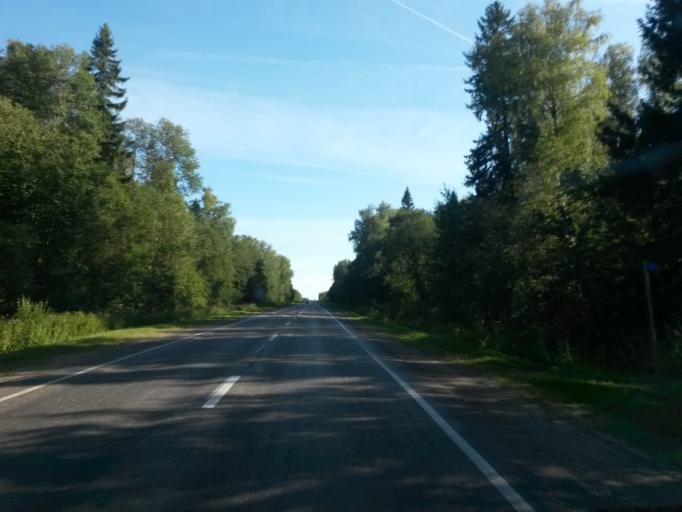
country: RU
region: Jaroslavl
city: Gavrilov-Yam
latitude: 57.4198
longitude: 39.9196
